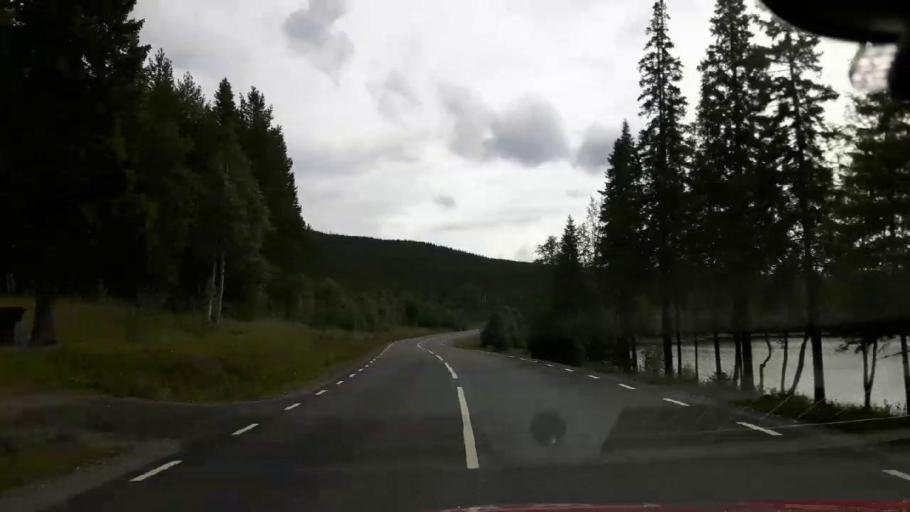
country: NO
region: Nord-Trondelag
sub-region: Lierne
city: Sandvika
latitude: 64.6469
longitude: 14.1406
